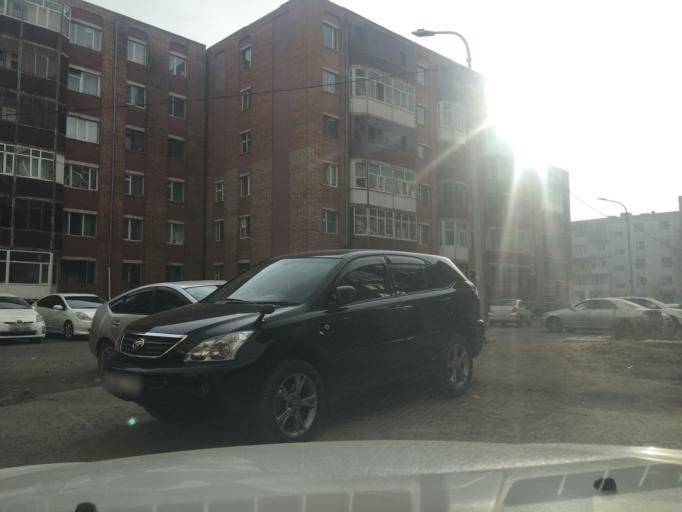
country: MN
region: Ulaanbaatar
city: Ulaanbaatar
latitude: 47.9136
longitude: 106.8739
